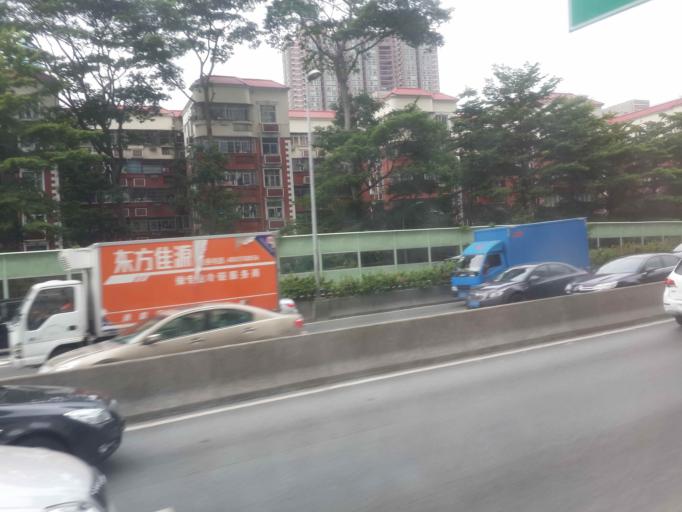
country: CN
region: Guangdong
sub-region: Shenzhen
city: Shenzhen
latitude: 22.5370
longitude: 114.1072
